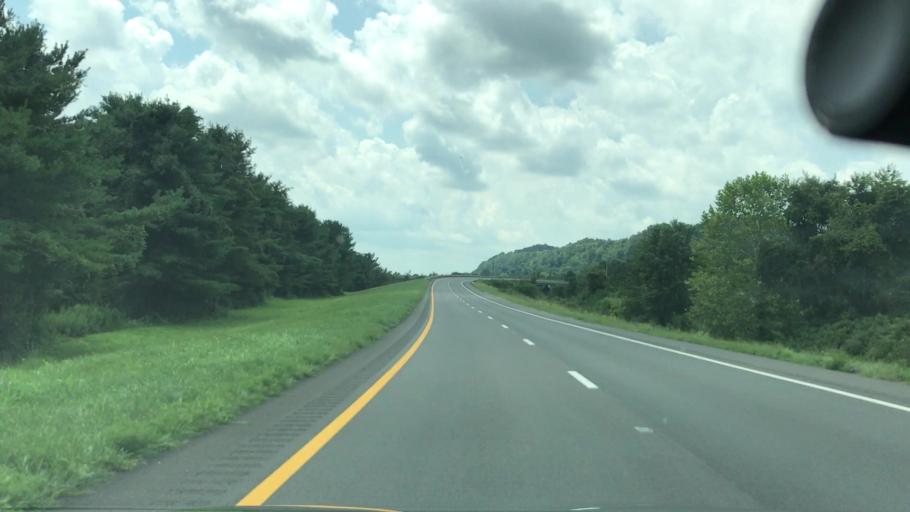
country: US
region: West Virginia
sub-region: Mason County
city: Point Pleasant
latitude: 38.8405
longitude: -82.1594
